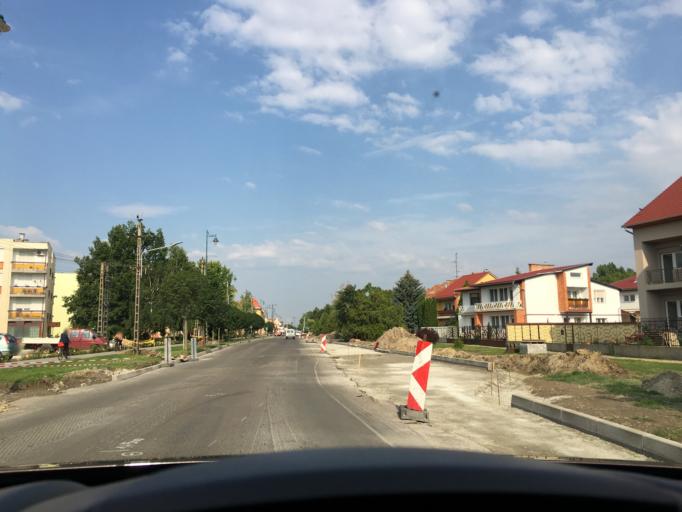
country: HU
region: Csongrad
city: Morahalom
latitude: 46.2160
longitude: 19.8948
